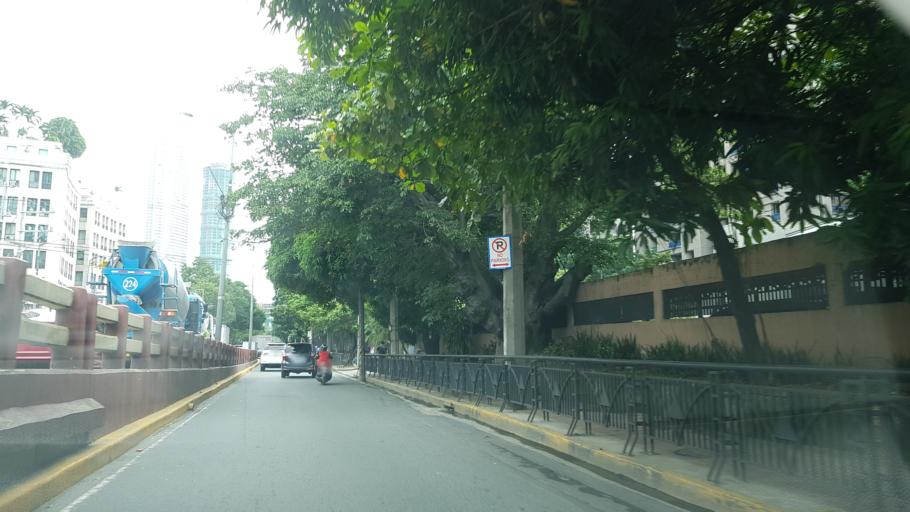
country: PH
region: Metro Manila
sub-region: Pasig
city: Pasig City
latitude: 14.5827
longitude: 121.0637
